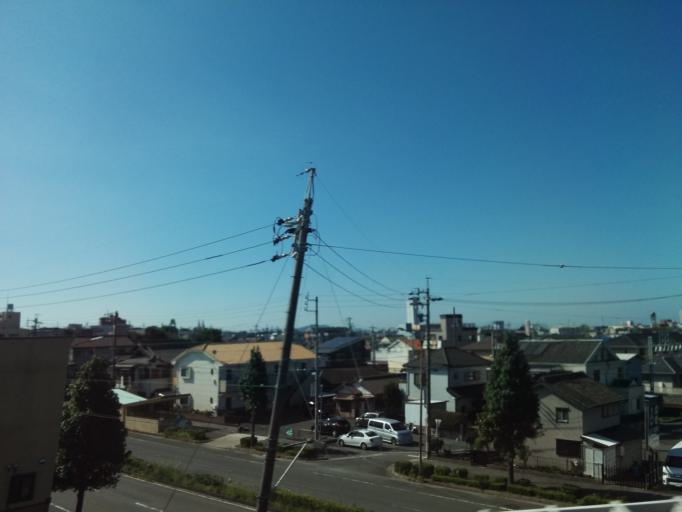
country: JP
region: Aichi
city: Toyohashi
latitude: 34.7495
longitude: 137.3896
